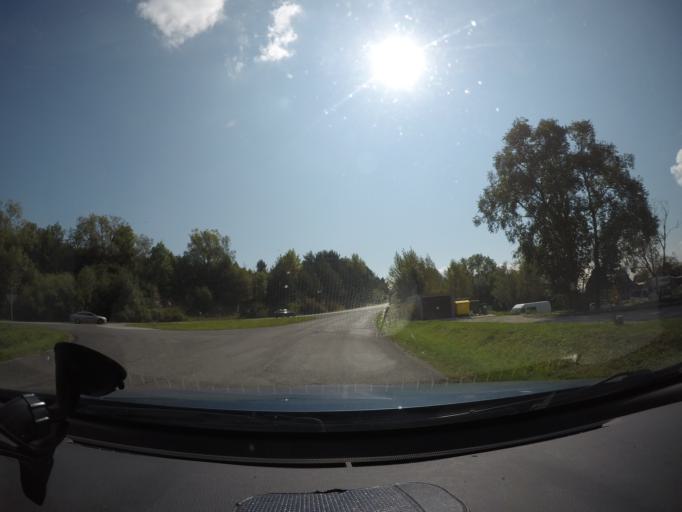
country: SK
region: Zilinsky
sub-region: Okres Liptovsky Mikulas
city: Liptovsky Mikulas
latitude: 49.1351
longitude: 19.5152
